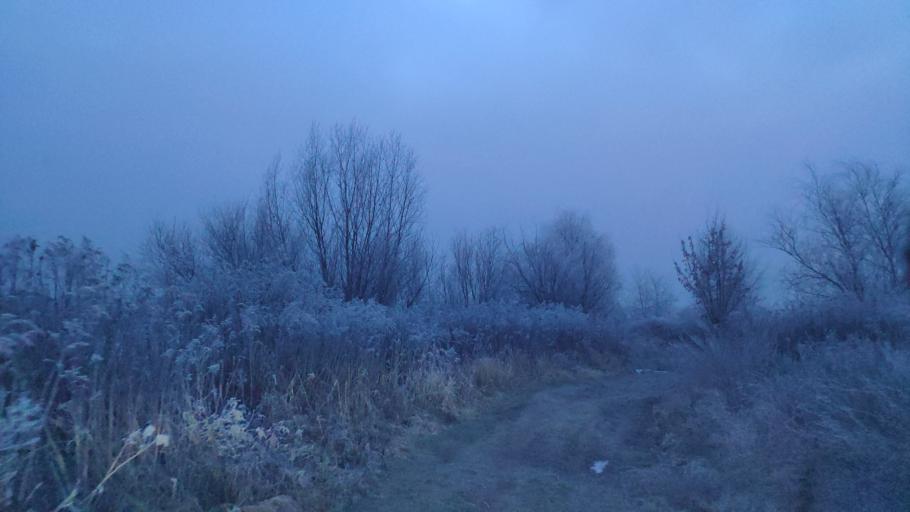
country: SK
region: Kosicky
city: Kosice
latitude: 48.6134
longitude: 21.3353
